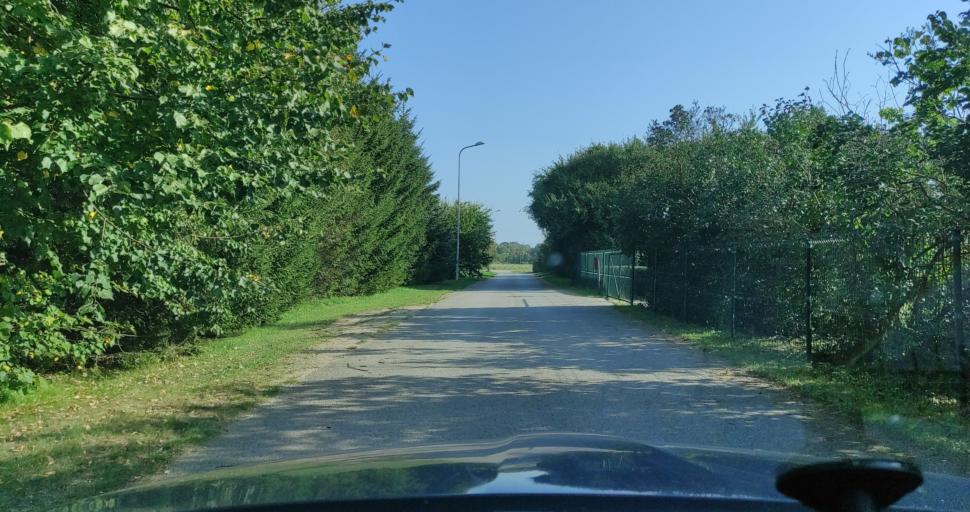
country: LV
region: Ventspils Rajons
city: Piltene
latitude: 57.2307
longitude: 21.6119
